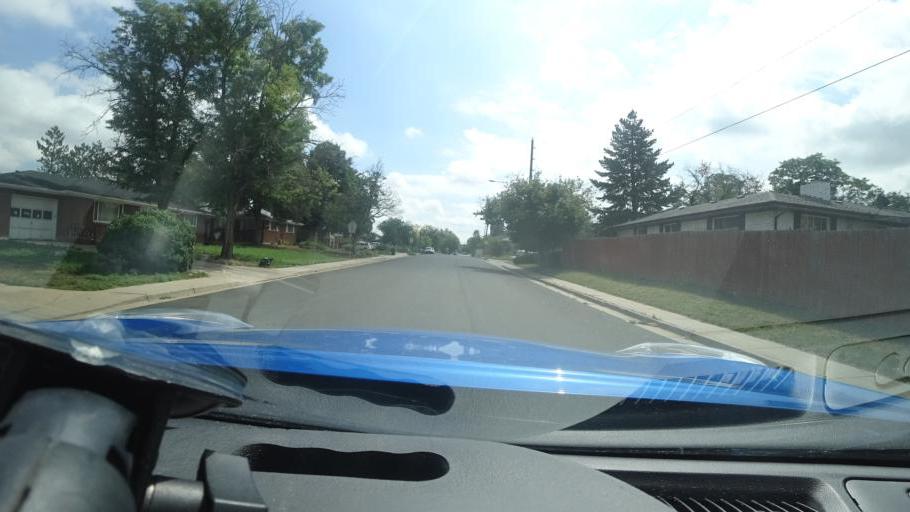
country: US
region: Colorado
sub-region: Adams County
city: Aurora
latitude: 39.7251
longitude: -104.8588
